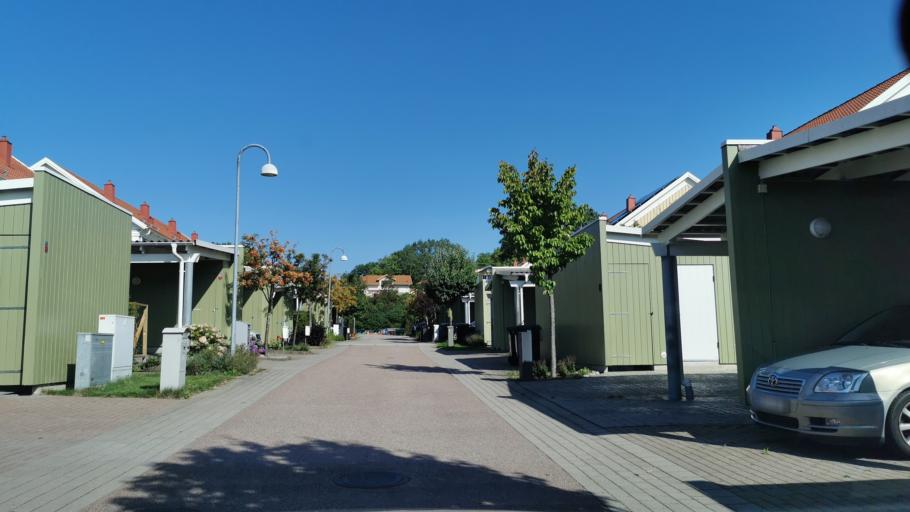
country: SE
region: Vaestra Goetaland
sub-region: Molndal
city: Moelndal
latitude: 57.6511
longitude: 11.9675
